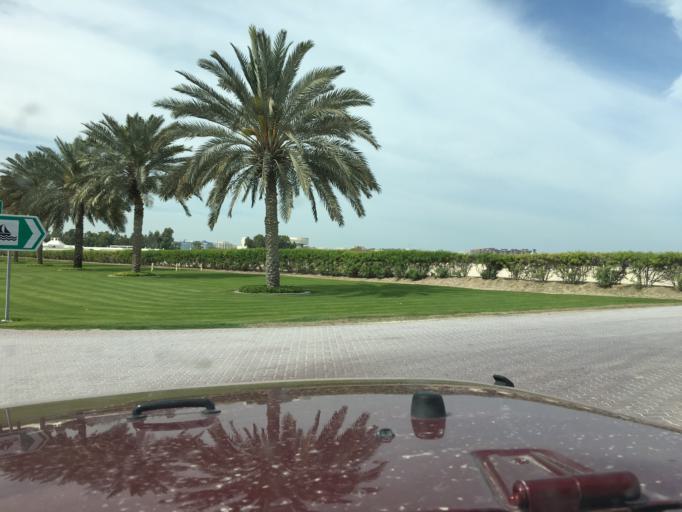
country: AE
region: Dubai
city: Dubai
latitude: 25.1144
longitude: 55.1707
